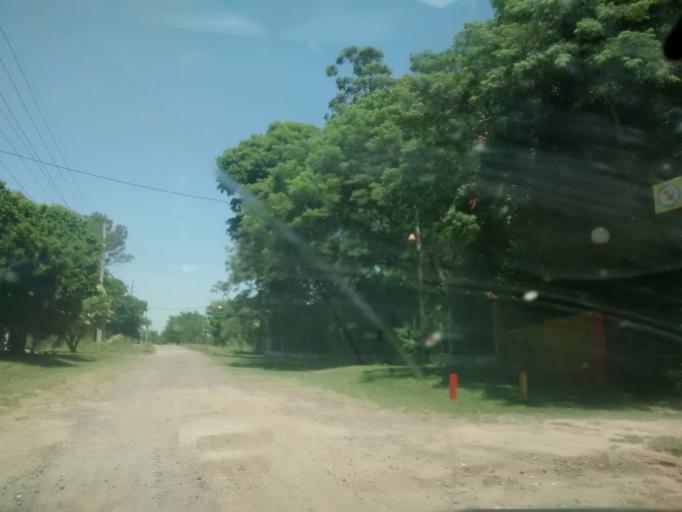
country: AR
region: Chaco
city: Fontana
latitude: -27.4187
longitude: -58.9845
